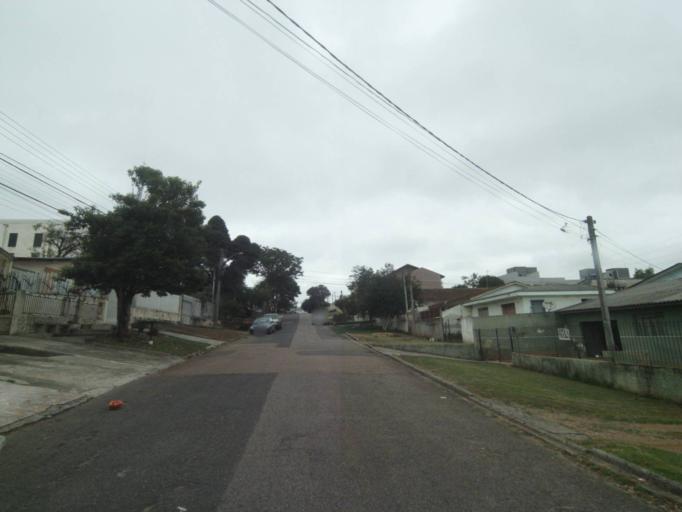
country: BR
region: Parana
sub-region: Sao Jose Dos Pinhais
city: Sao Jose dos Pinhais
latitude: -25.5375
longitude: -49.2829
